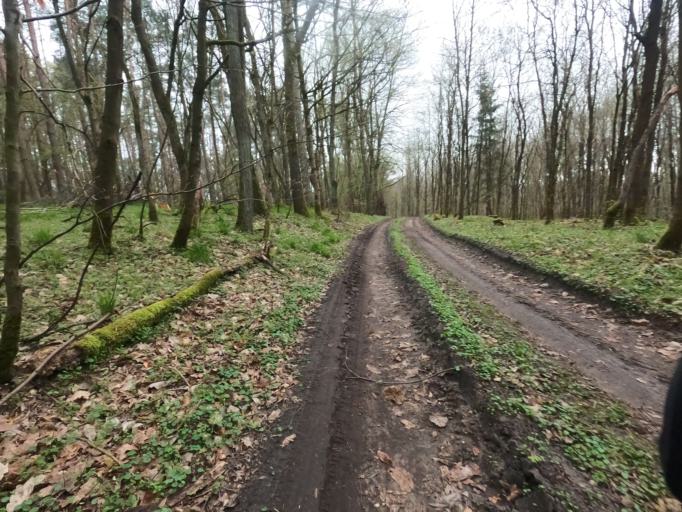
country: PL
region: West Pomeranian Voivodeship
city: Trzcinsko Zdroj
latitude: 52.9171
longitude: 14.6117
